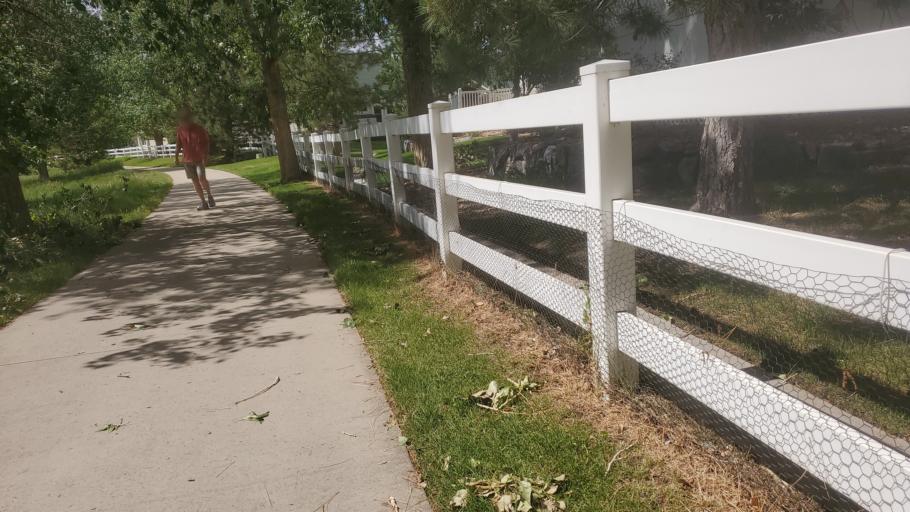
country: US
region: Colorado
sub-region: Adams County
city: Aurora
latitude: 39.6687
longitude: -104.8392
